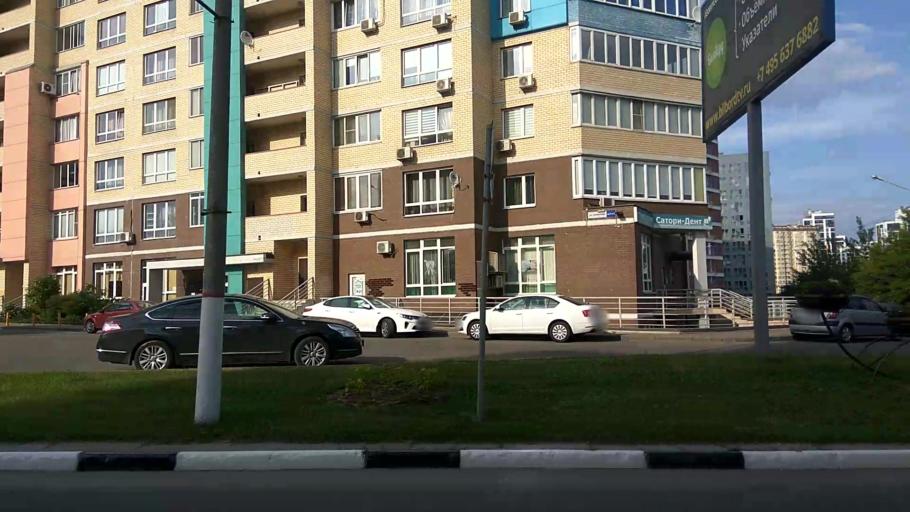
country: RU
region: Moskovskaya
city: Mytishchi
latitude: 55.9173
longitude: 37.7464
